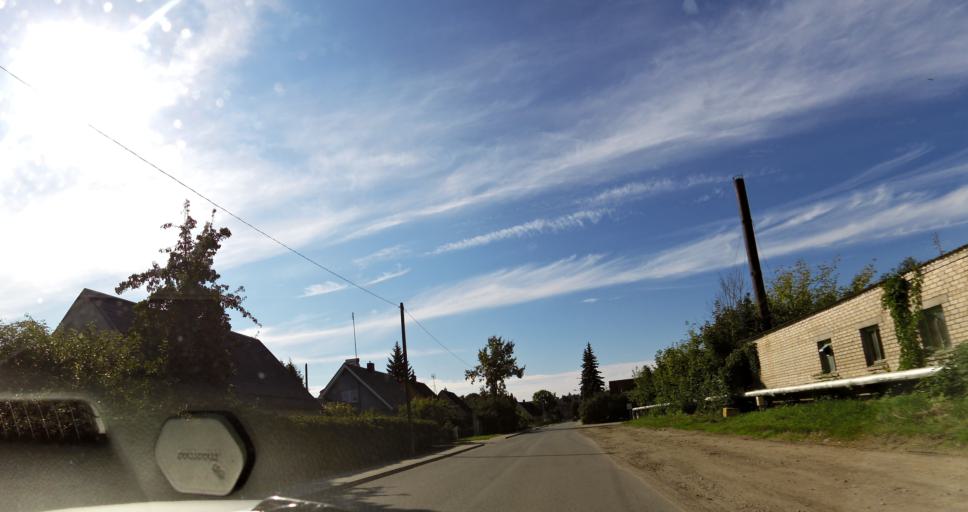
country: LT
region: Panevezys
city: Pasvalys
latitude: 56.0651
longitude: 24.3969
